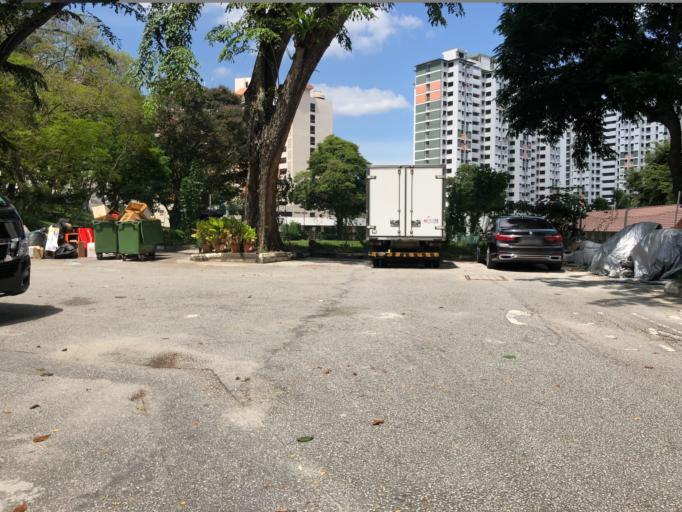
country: SG
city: Singapore
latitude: 1.2855
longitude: 103.8417
